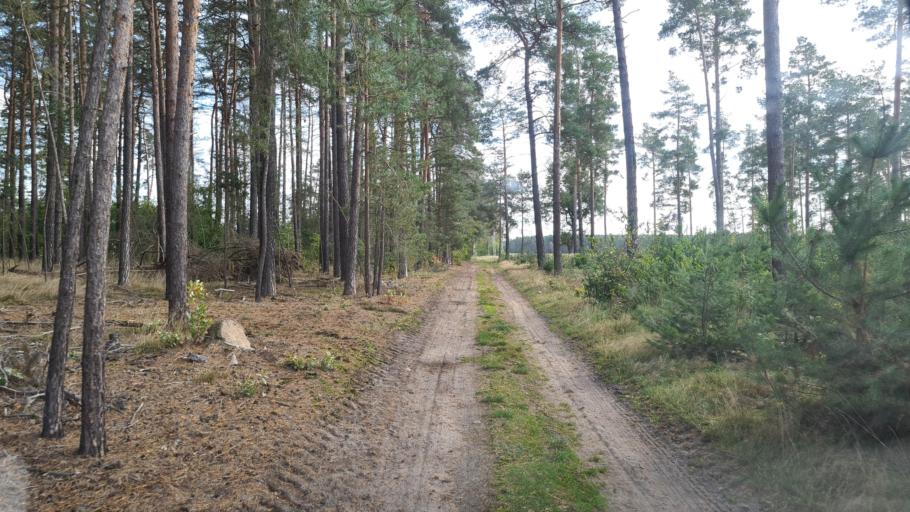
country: DE
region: Brandenburg
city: Bronkow
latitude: 51.7315
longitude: 13.8642
